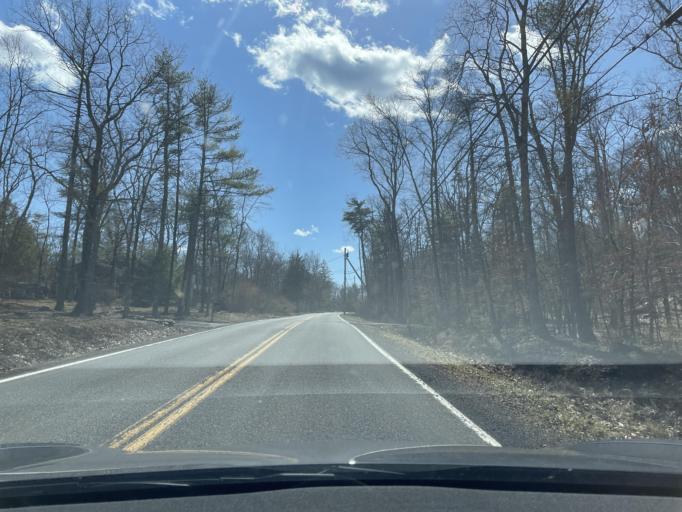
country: US
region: New York
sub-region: Ulster County
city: West Hurley
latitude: 41.9675
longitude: -74.0990
